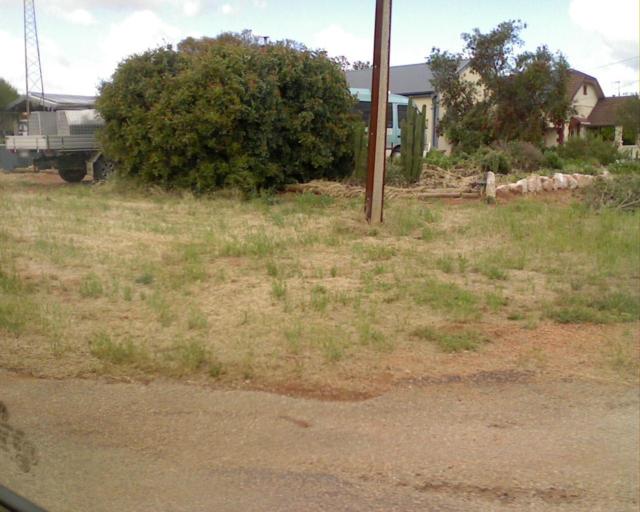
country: AU
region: South Australia
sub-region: Port Pirie City and Dists
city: Solomontown
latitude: -33.0312
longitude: 138.2714
